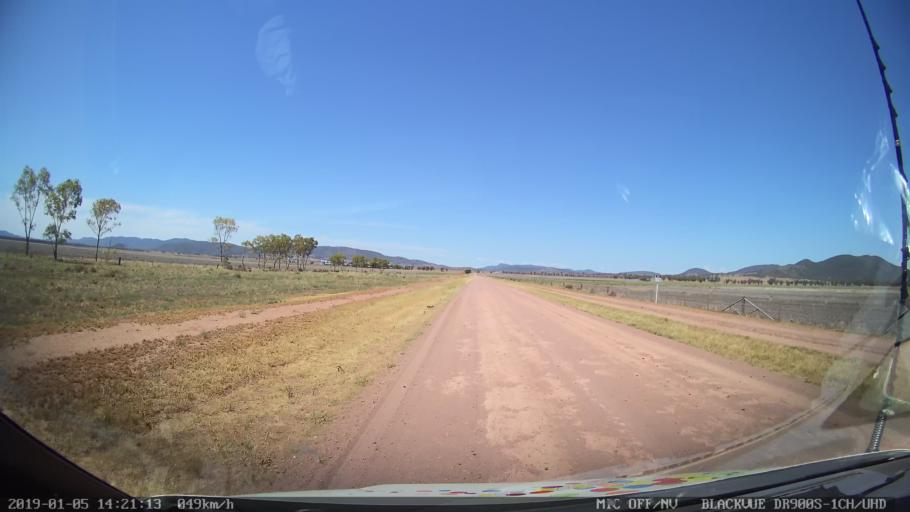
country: AU
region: New South Wales
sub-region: Liverpool Plains
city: Quirindi
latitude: -31.2468
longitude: 150.5116
